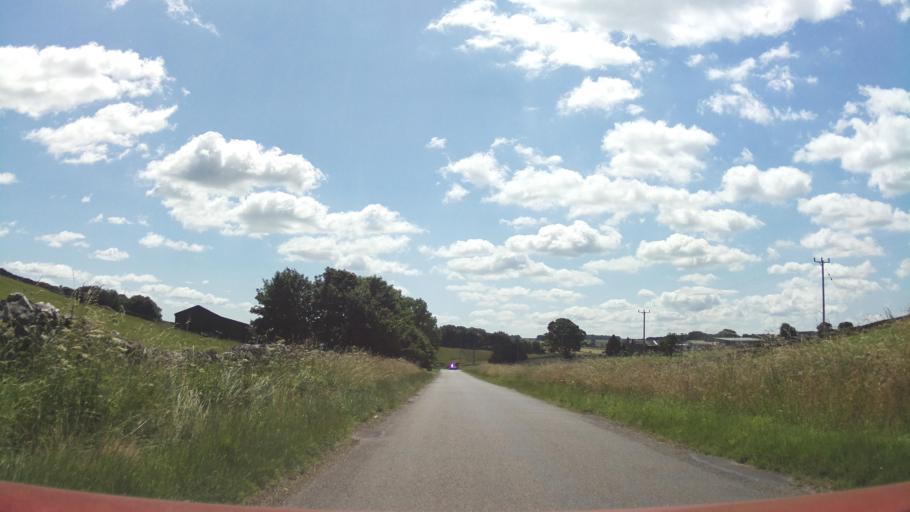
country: GB
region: England
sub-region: Derbyshire
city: Tideswell
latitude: 53.2128
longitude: -1.7808
